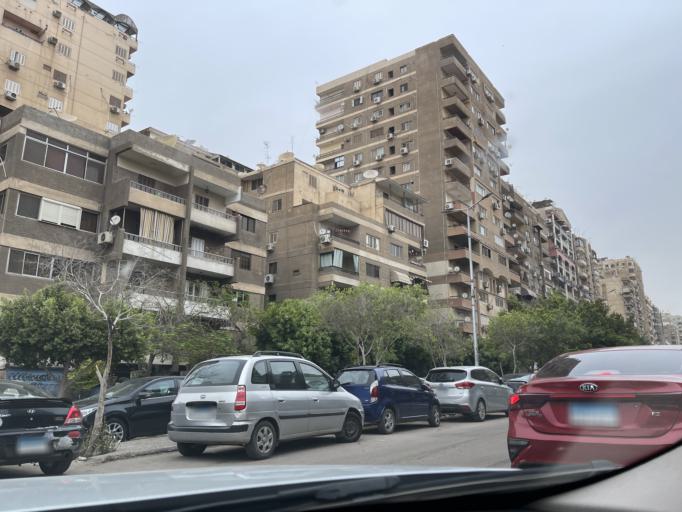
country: EG
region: Muhafazat al Qahirah
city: Cairo
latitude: 30.0599
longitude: 31.3500
